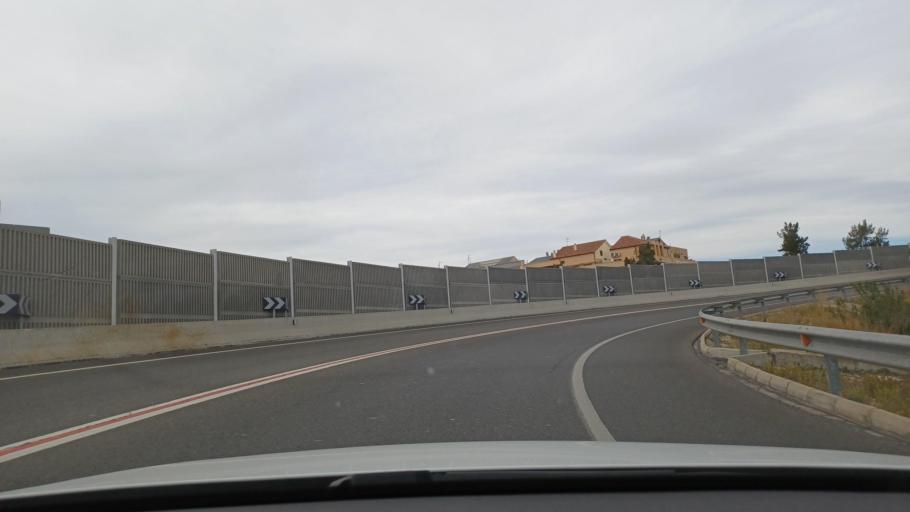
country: ES
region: Valencia
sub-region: Provincia de Valencia
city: Picassent
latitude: 39.3677
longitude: -0.4555
